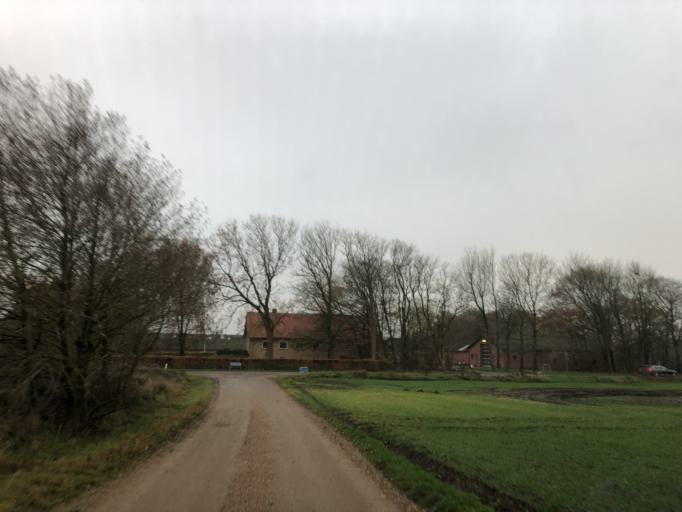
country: DK
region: Central Jutland
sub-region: Herning Kommune
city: Vildbjerg
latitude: 56.2049
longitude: 8.7231
